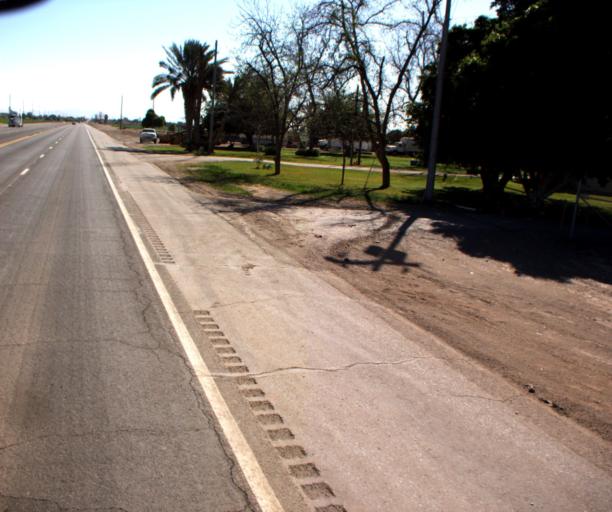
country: US
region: Arizona
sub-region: Yuma County
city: Somerton
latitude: 32.5966
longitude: -114.7346
